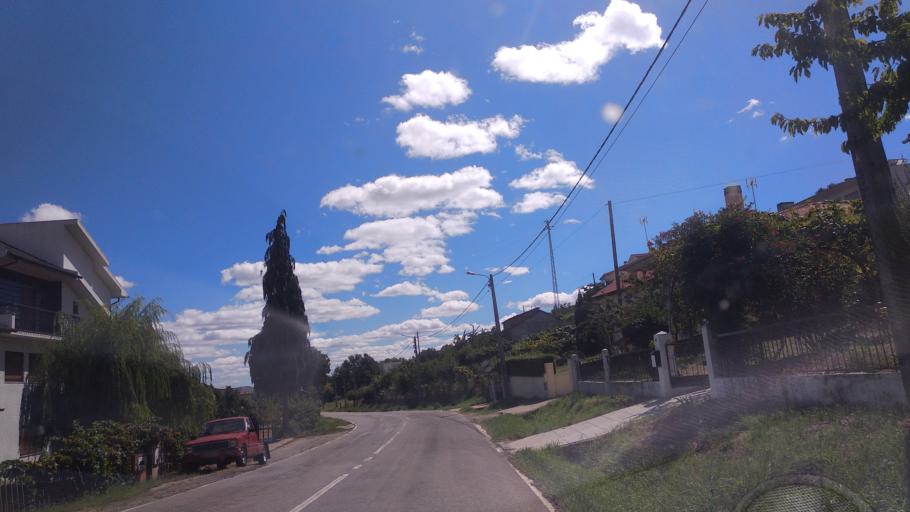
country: PT
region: Braganca
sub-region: Braganca Municipality
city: Braganca
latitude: 41.7775
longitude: -6.7628
